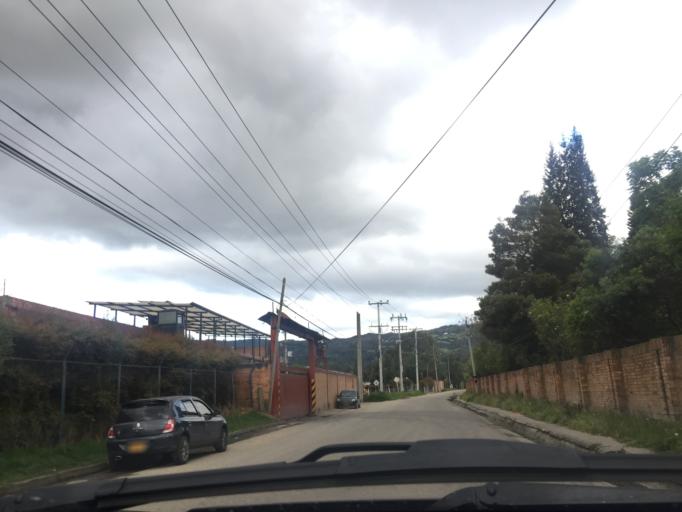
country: CO
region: Cundinamarca
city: Sopo
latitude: 4.9412
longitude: -73.9532
